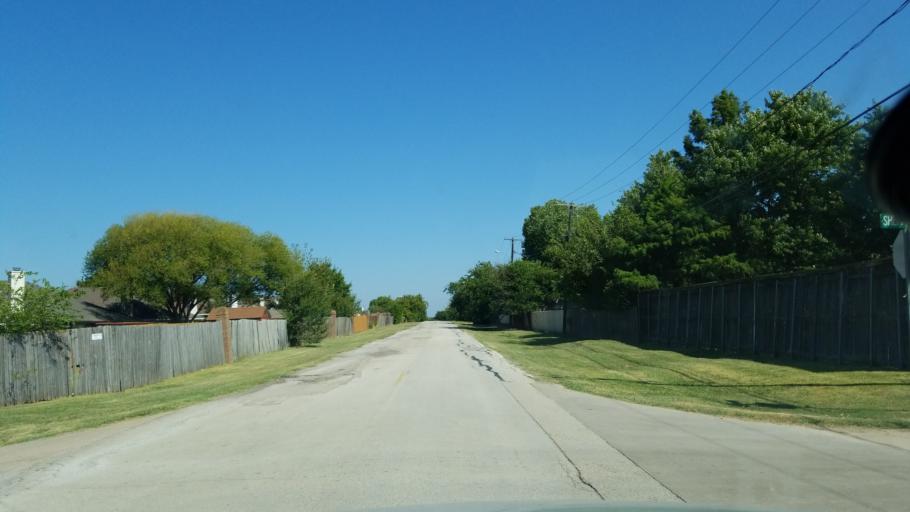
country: US
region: Texas
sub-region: Tarrant County
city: Mansfield
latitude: 32.5541
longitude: -97.1338
